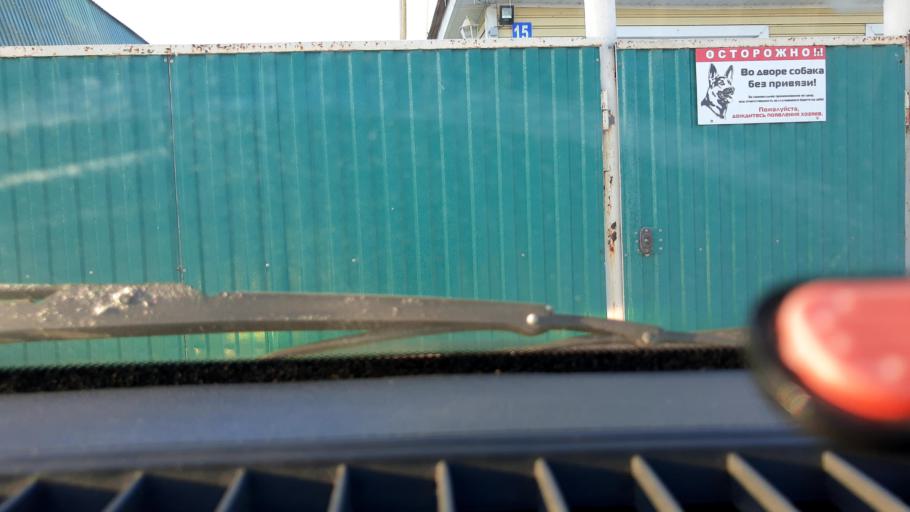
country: RU
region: Bashkortostan
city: Mikhaylovka
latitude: 54.8706
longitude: 55.7592
